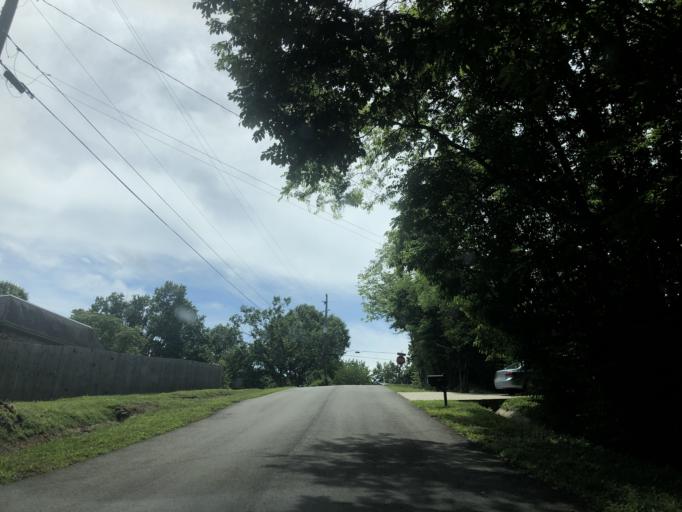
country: US
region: Tennessee
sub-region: Davidson County
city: Belle Meade
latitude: 36.0800
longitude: -86.9316
